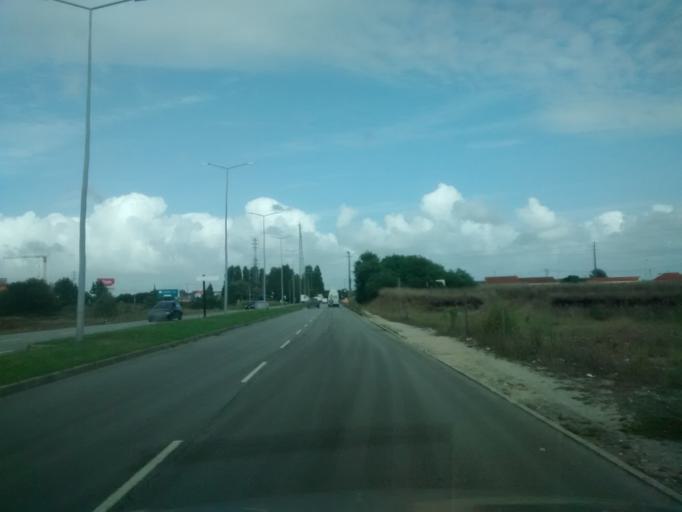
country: PT
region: Aveiro
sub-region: Aveiro
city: Aveiro
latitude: 40.6406
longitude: -8.6356
